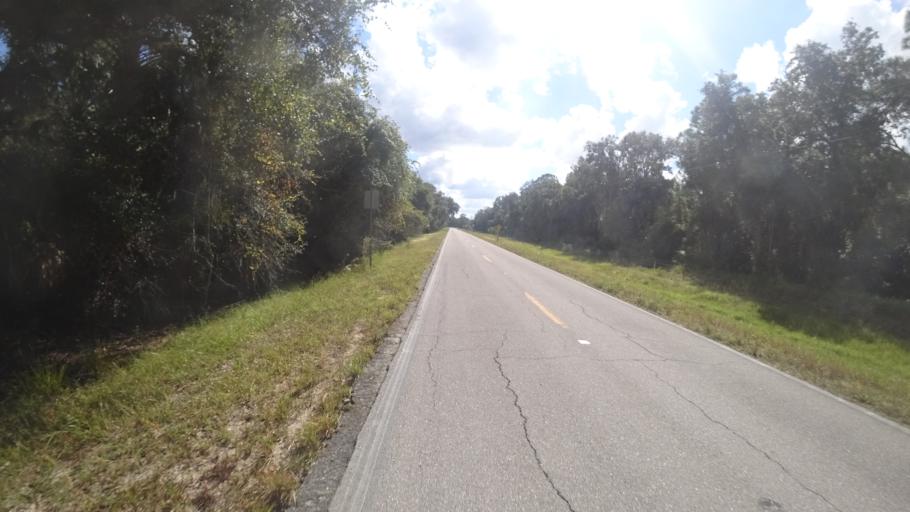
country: US
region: Florida
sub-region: Sarasota County
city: North Port
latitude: 27.2216
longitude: -82.1221
